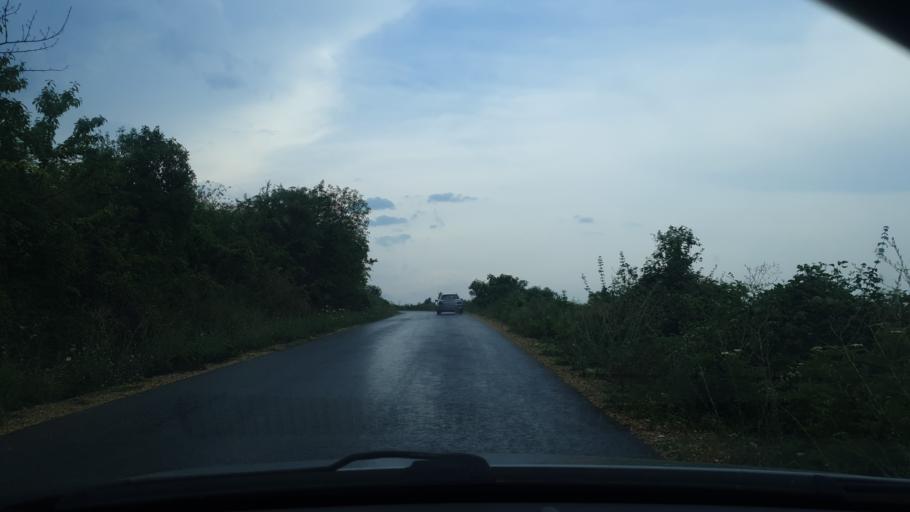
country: RS
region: Central Serbia
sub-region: Sumadijski Okrug
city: Kragujevac
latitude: 44.0634
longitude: 20.7864
